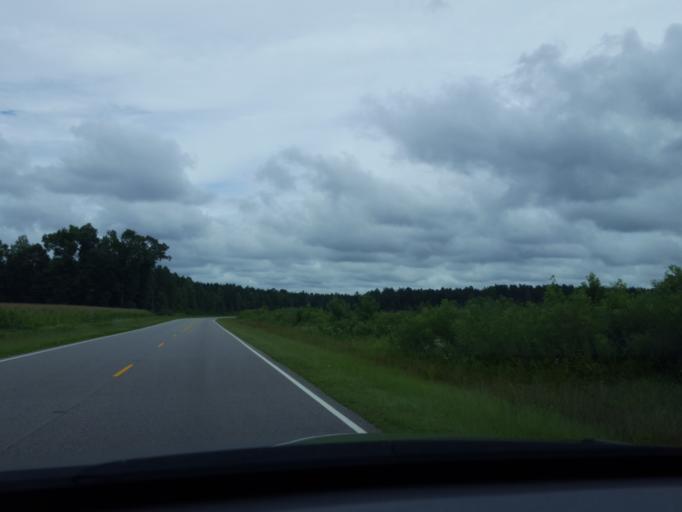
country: US
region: North Carolina
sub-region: Martin County
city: Williamston
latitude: 35.7493
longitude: -76.9813
